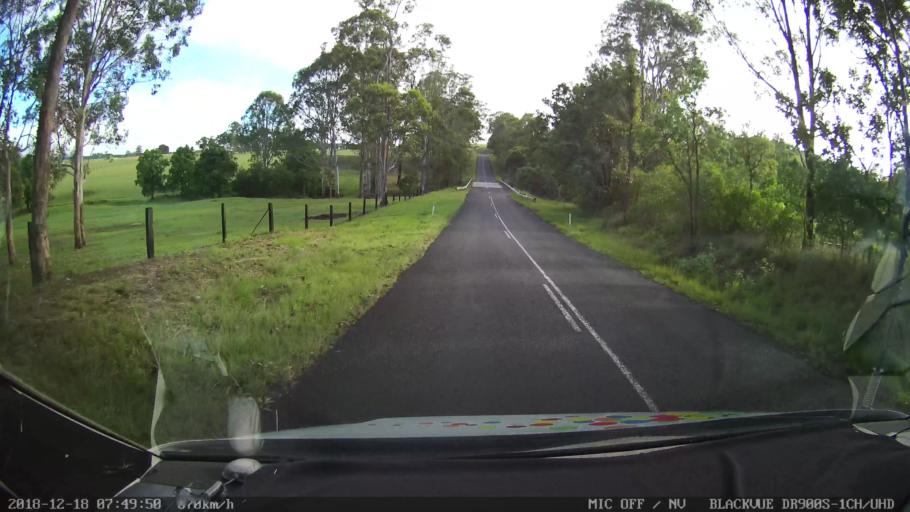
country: AU
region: New South Wales
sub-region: Kyogle
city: Kyogle
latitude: -28.4506
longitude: 152.5714
